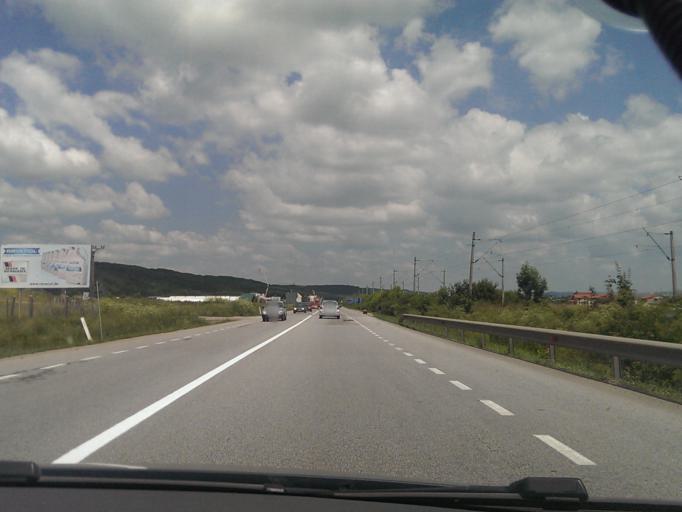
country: RO
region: Cluj
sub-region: Comuna Apahida
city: Apahida
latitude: 46.8235
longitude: 23.7447
